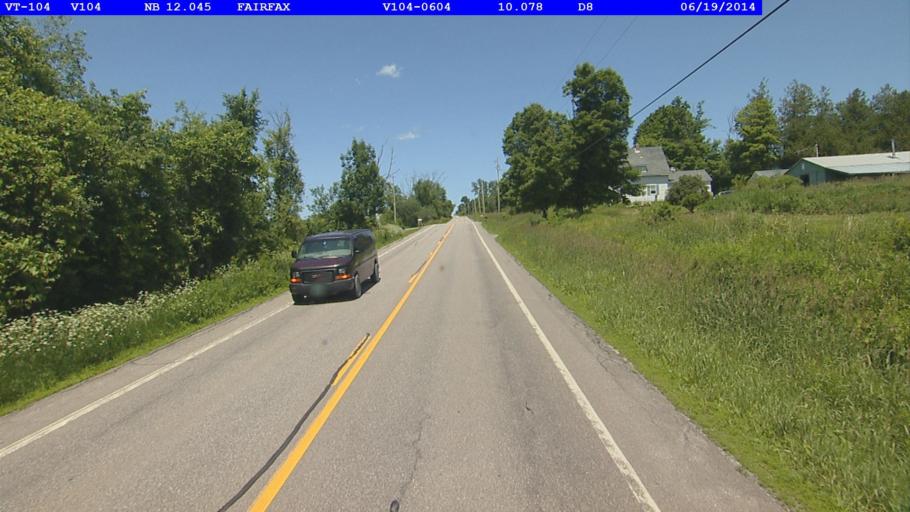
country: US
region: Vermont
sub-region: Franklin County
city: Saint Albans
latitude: 44.7293
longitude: -73.0458
